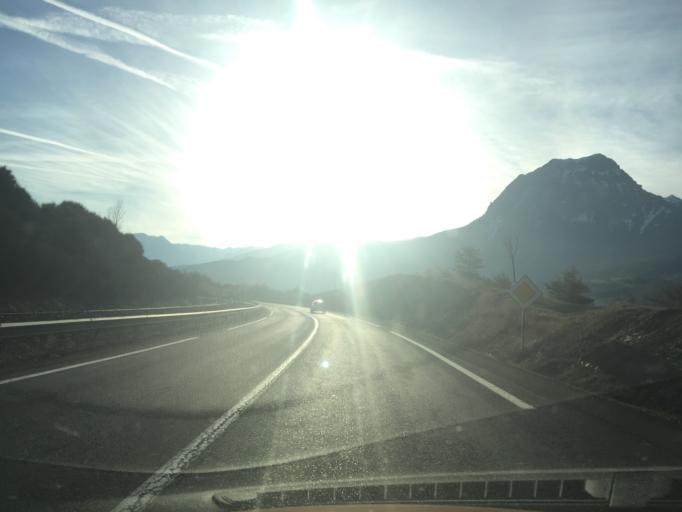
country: FR
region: Provence-Alpes-Cote d'Azur
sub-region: Departement des Hautes-Alpes
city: Chorges
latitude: 44.5239
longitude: 6.3428
